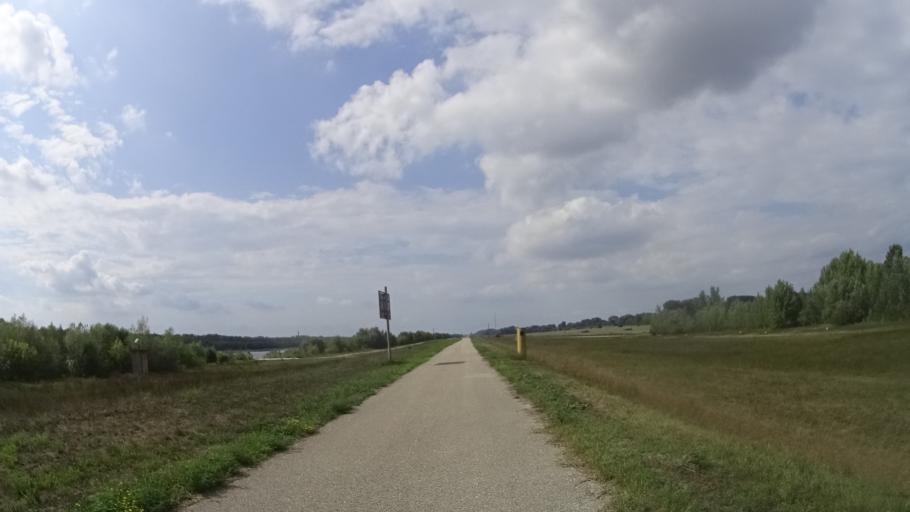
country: SK
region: Trnavsky
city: Gabcikovo
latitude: 47.8233
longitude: 17.6099
